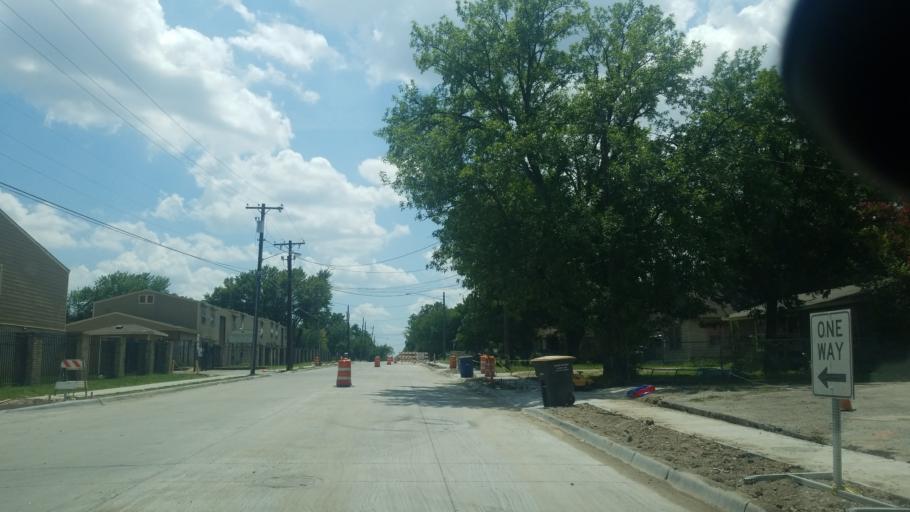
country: US
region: Texas
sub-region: Dallas County
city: Dallas
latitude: 32.7143
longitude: -96.7664
